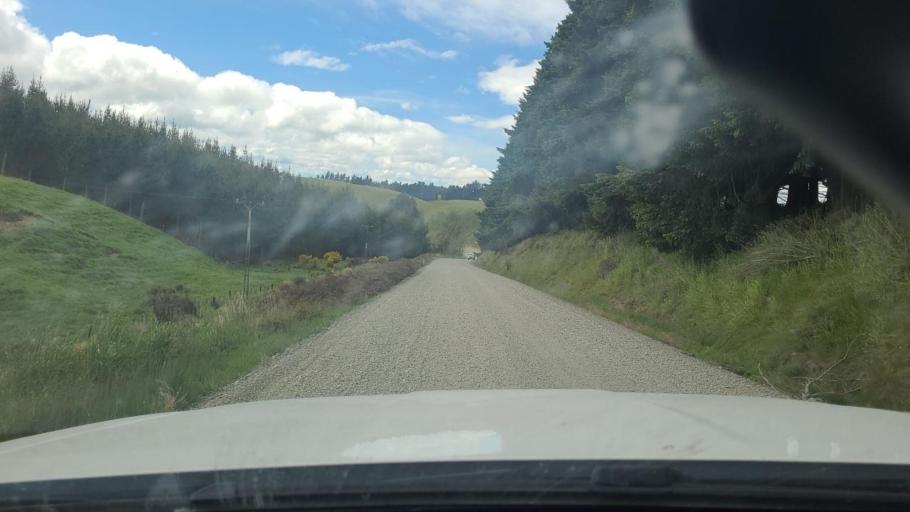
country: NZ
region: Southland
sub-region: Southland District
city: Te Anau
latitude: -45.4896
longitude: 167.8301
